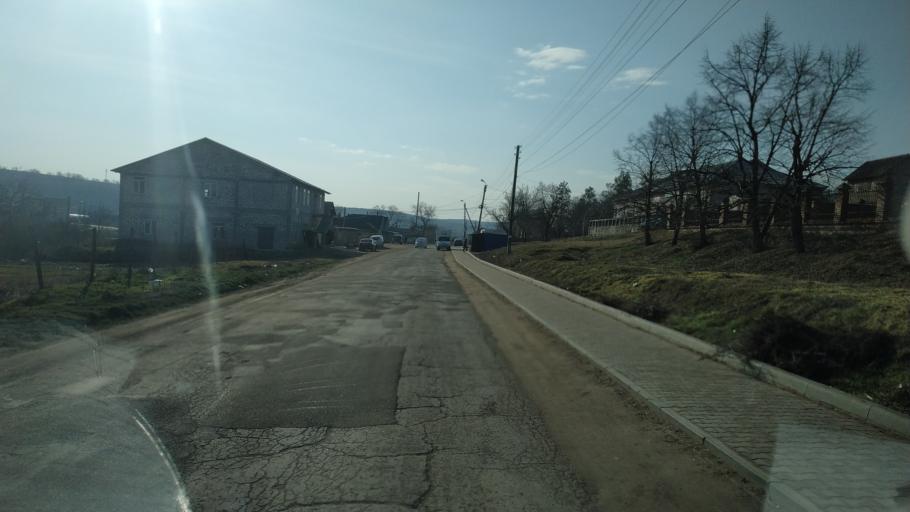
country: MD
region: Chisinau
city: Singera
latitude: 46.8247
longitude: 29.0363
